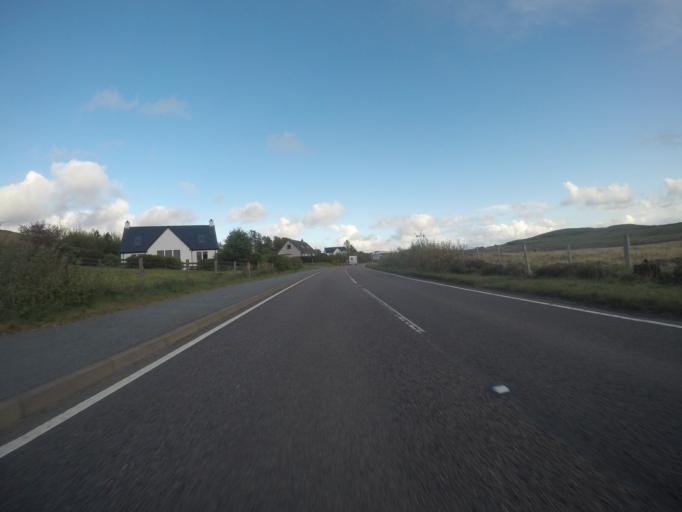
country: GB
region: Scotland
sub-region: Highland
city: Portree
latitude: 57.4812
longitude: -6.3018
